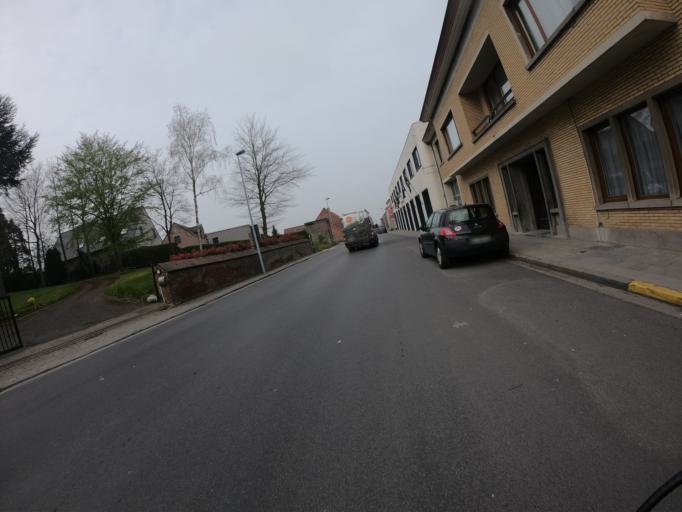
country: BE
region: Flanders
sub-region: Provincie West-Vlaanderen
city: Zwevegem
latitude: 50.8155
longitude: 3.3747
